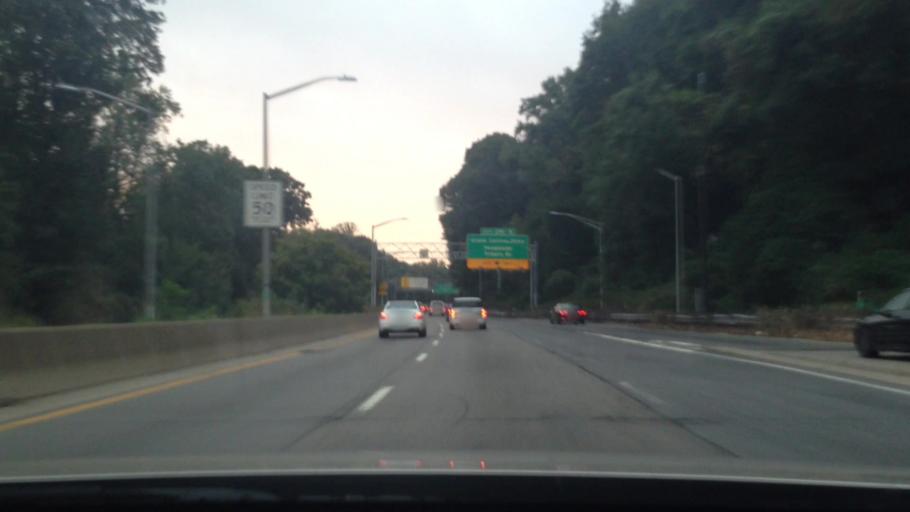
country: US
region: New York
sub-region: Nassau County
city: Lake Success
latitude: 40.7502
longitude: -73.7412
